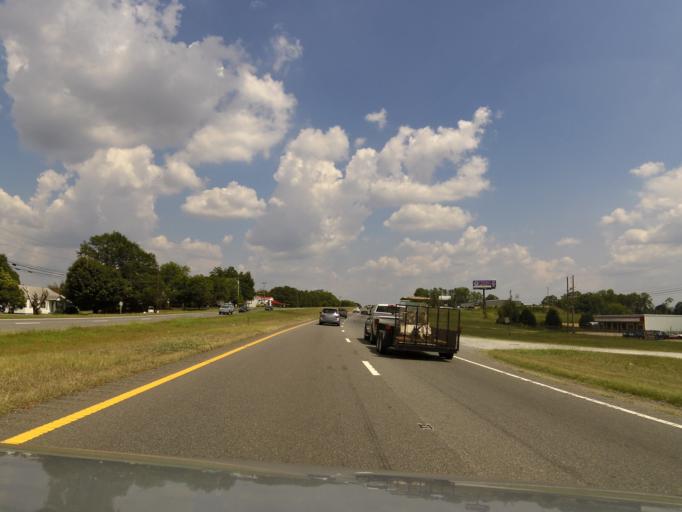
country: US
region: North Carolina
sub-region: Cleveland County
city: White Plains
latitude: 35.2472
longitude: -81.4338
